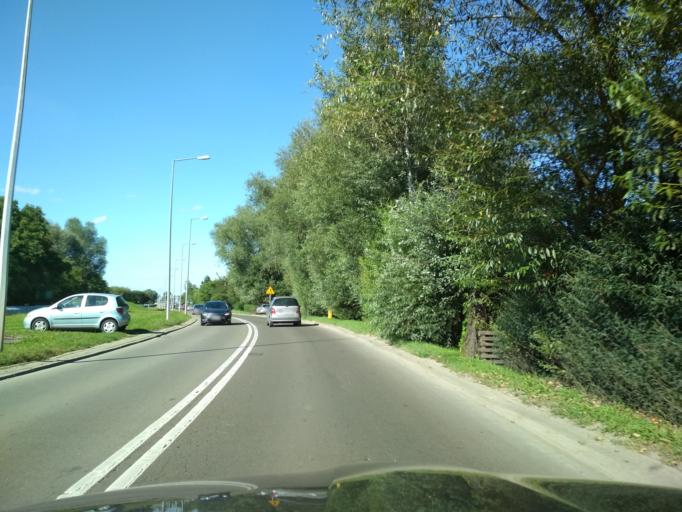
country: PL
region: Subcarpathian Voivodeship
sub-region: Rzeszow
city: Rzeszow
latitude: 50.0522
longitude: 22.0205
